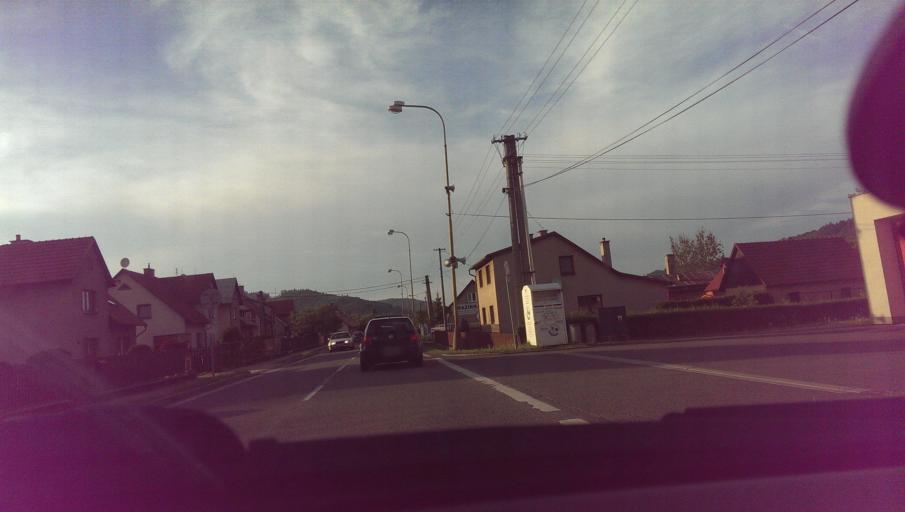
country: CZ
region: Zlin
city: Valasska Polanka
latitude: 49.2628
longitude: 17.9967
